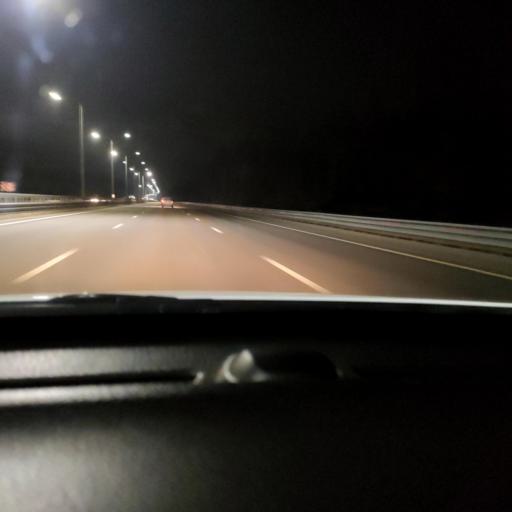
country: RU
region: Voronezj
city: Somovo
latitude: 51.7031
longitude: 39.3057
